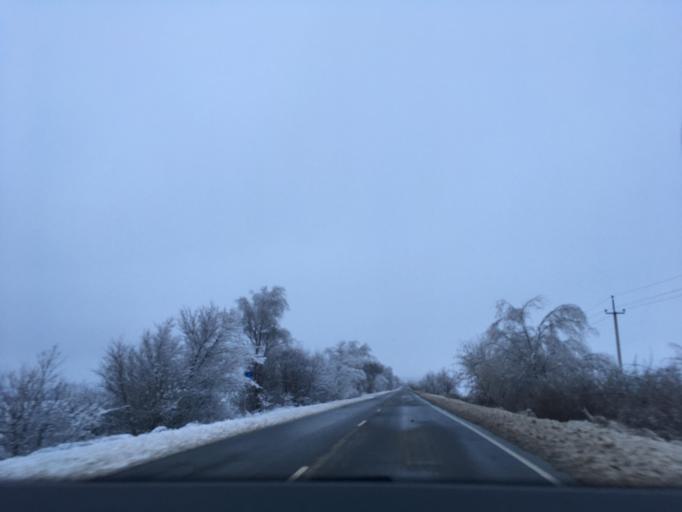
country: RU
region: Voronezj
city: Verkhniy Mamon
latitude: 50.0203
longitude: 40.1095
